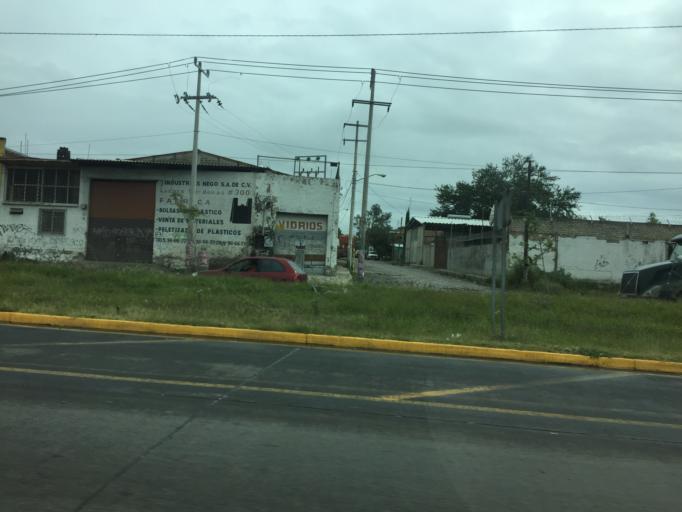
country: MX
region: Jalisco
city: Tlaquepaque
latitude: 20.6272
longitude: -103.3001
